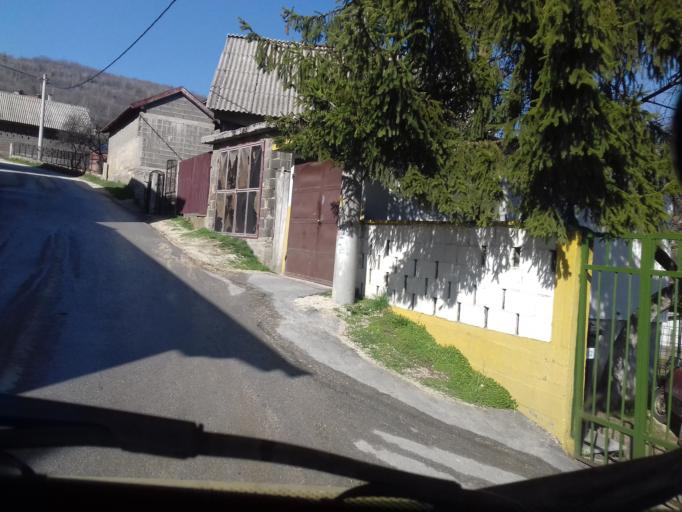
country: BA
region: Federation of Bosnia and Herzegovina
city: Travnik
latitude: 44.2552
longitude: 17.7345
